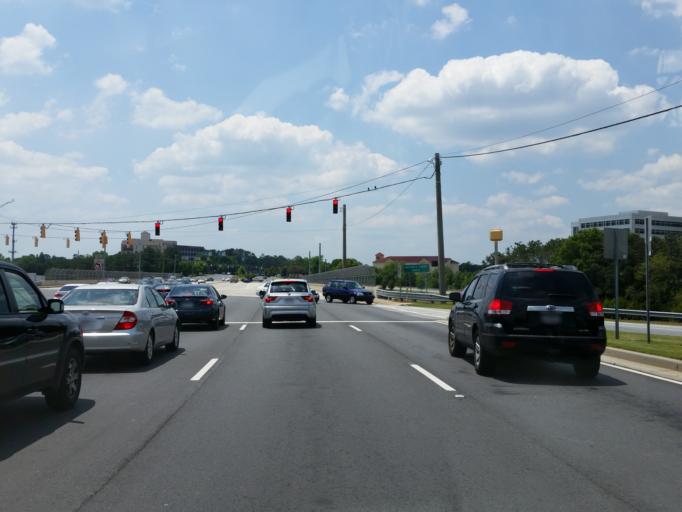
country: US
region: Georgia
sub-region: Cobb County
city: Vinings
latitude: 33.8653
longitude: -84.4781
